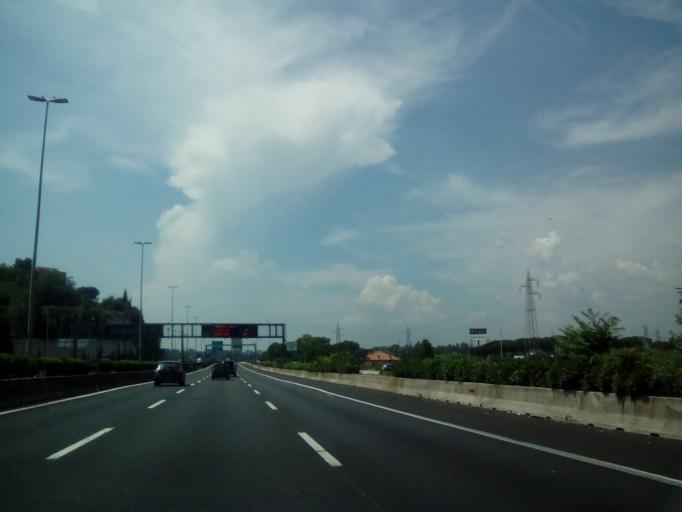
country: IT
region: Latium
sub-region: Citta metropolitana di Roma Capitale
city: Monte Caminetto
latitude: 41.9863
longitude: 12.5193
